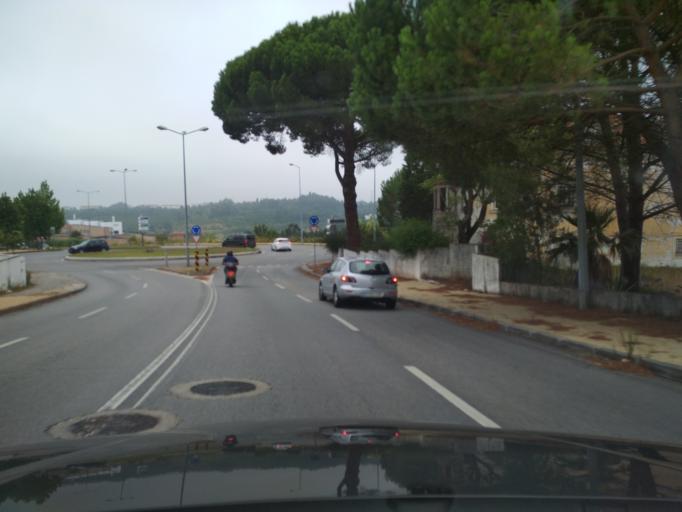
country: PT
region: Coimbra
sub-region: Coimbra
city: Coimbra
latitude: 40.2231
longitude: -8.4089
